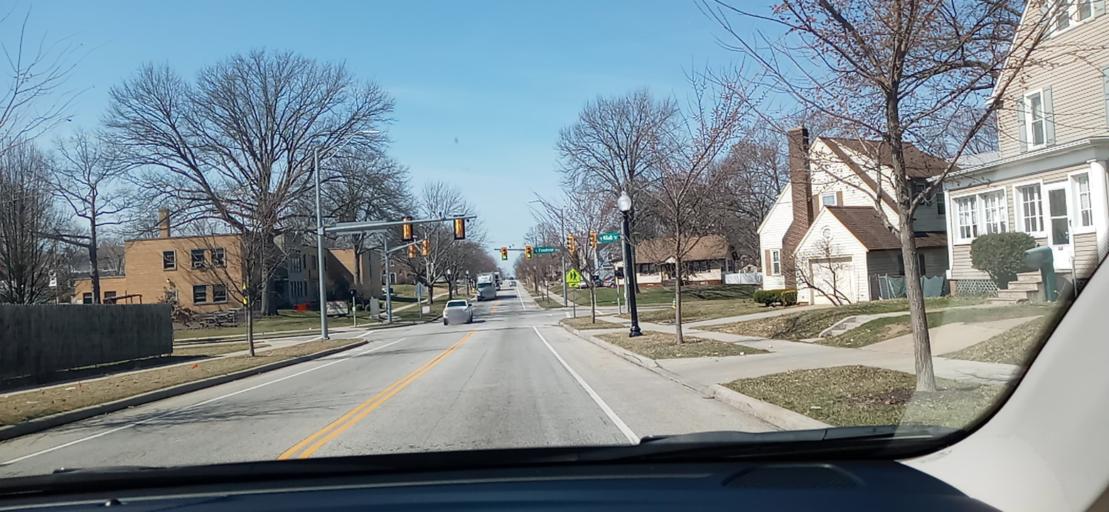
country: US
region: Ohio
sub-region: Summit County
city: Portage Lakes
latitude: 41.0399
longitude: -81.5132
